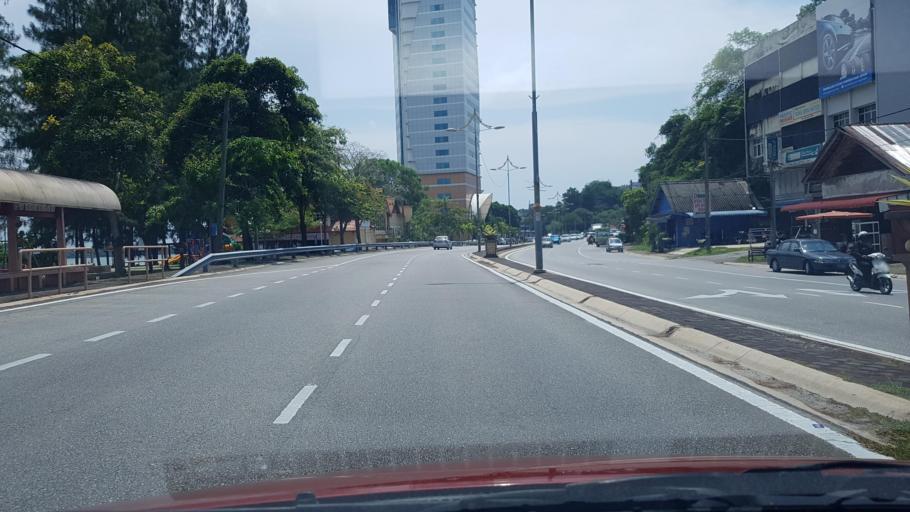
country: MY
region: Terengganu
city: Kuala Terengganu
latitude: 5.3269
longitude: 103.1325
